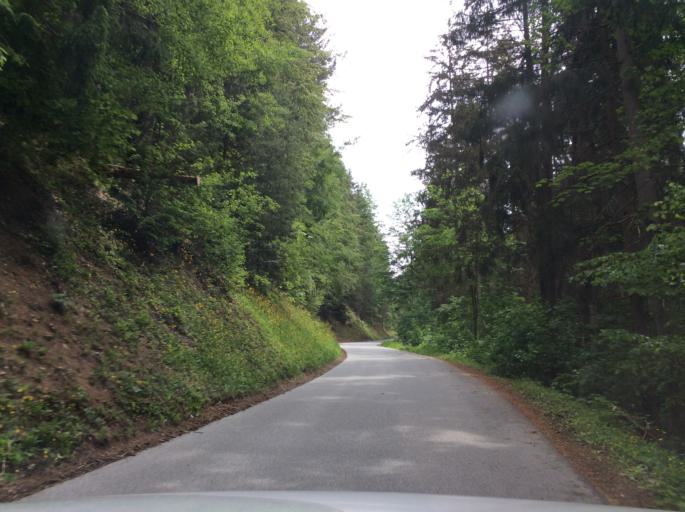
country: AT
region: Styria
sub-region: Politischer Bezirk Liezen
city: Schladming
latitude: 47.4095
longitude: 13.7218
